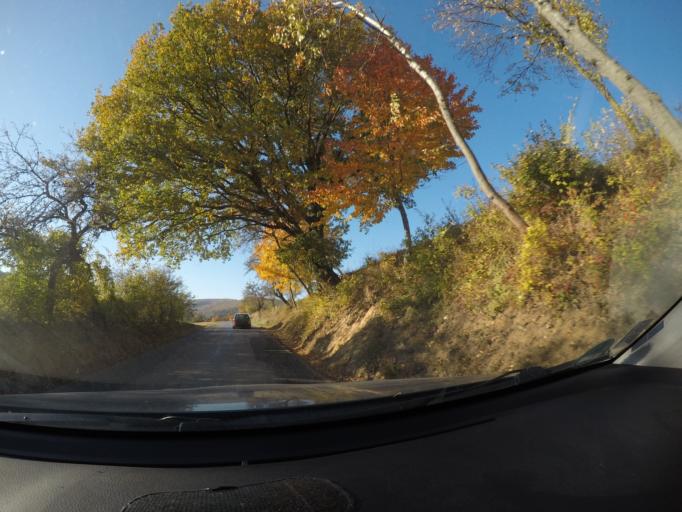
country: SK
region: Nitriansky
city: Nemsova
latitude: 48.9736
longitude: 18.0795
